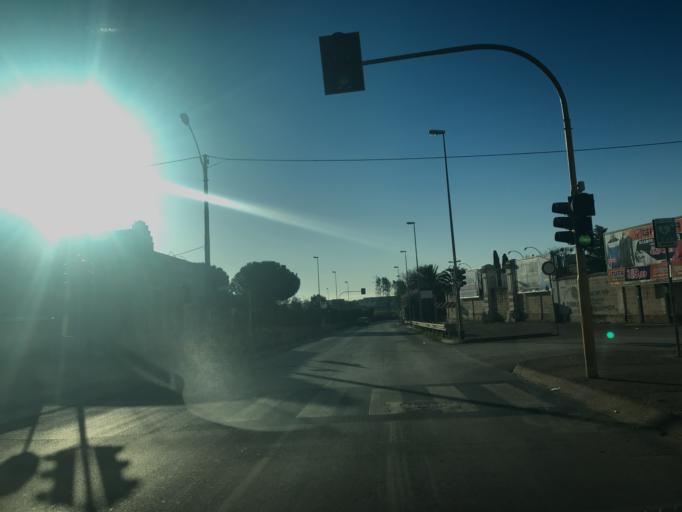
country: IT
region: Apulia
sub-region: Provincia di Bari
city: Corato
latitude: 41.1426
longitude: 16.4140
